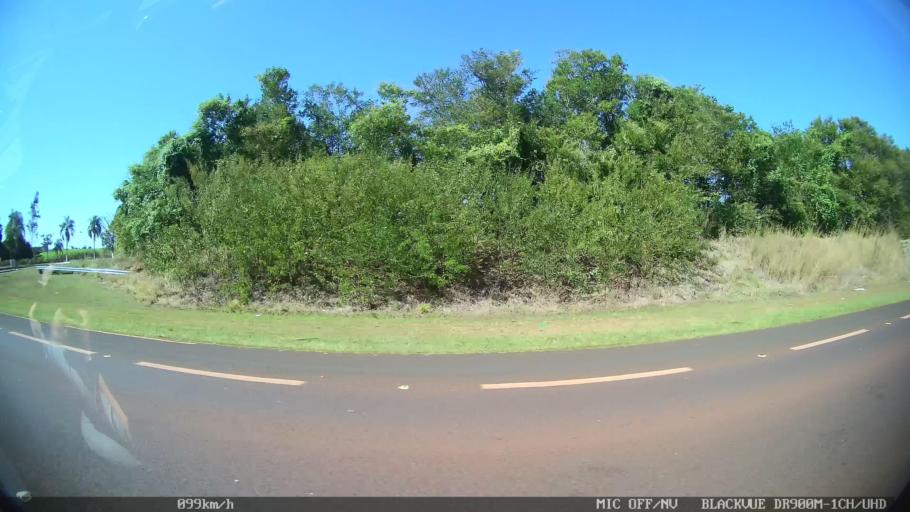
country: BR
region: Sao Paulo
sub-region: Franca
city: Franca
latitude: -20.6483
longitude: -47.4832
